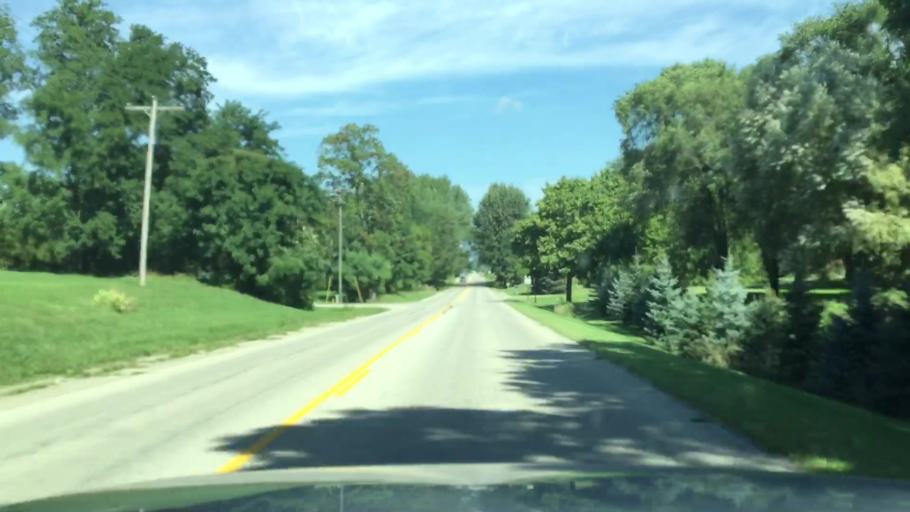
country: US
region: Michigan
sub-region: Lenawee County
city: Manitou Beach-Devils Lake
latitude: 42.0223
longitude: -84.2762
